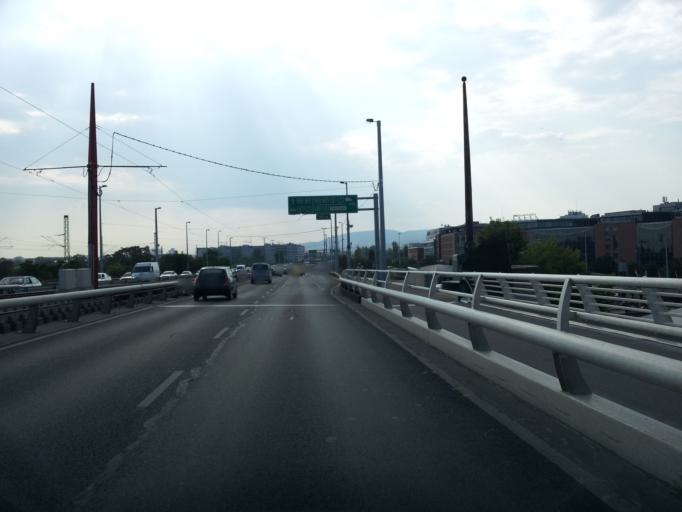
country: HU
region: Budapest
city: Budapest IX. keruelet
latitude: 47.4690
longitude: 19.0645
